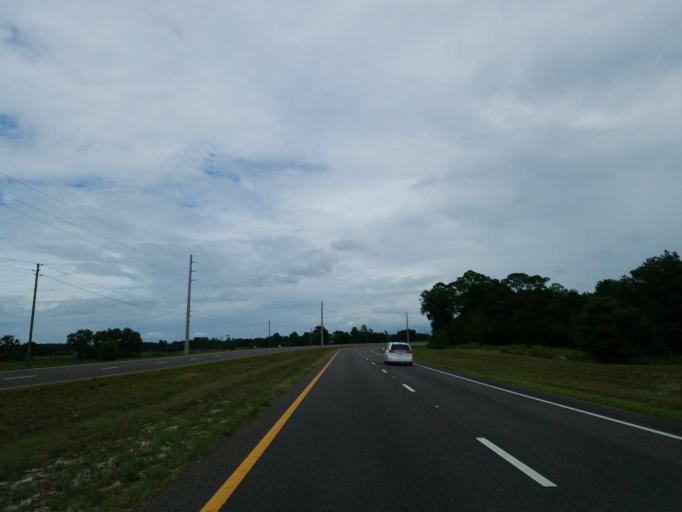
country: US
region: Florida
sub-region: Sumter County
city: Wildwood
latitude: 28.8787
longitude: -82.1283
